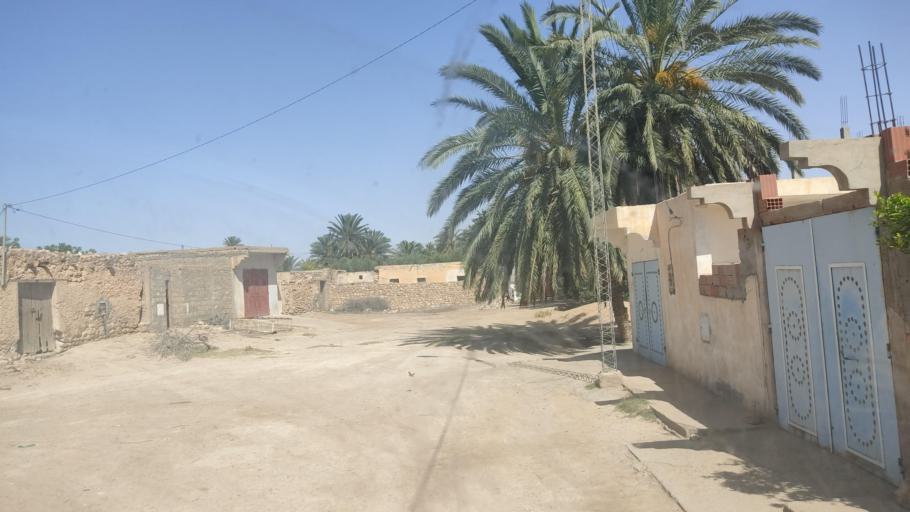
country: TN
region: Gafsa
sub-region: Gafsa Municipality
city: Gafsa
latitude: 34.3341
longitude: 8.9215
